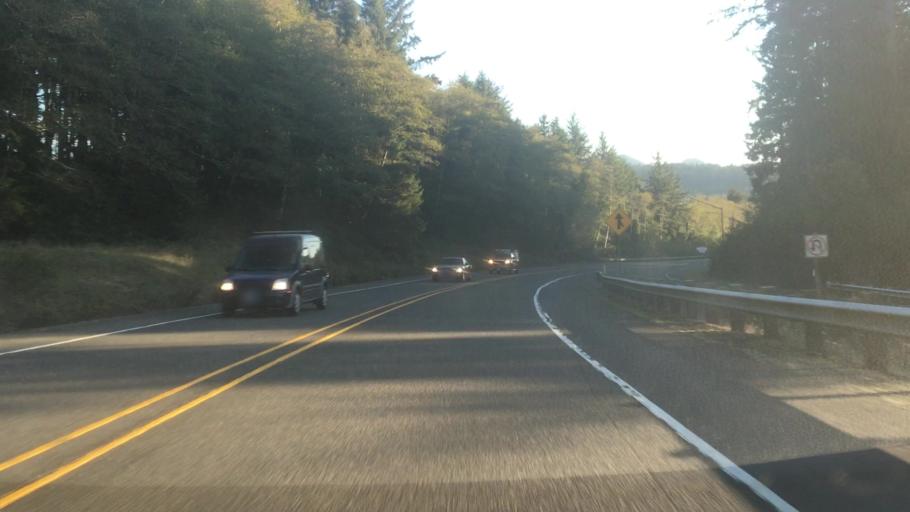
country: US
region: Oregon
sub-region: Clatsop County
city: Cannon Beach
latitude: 45.9029
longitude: -123.9532
